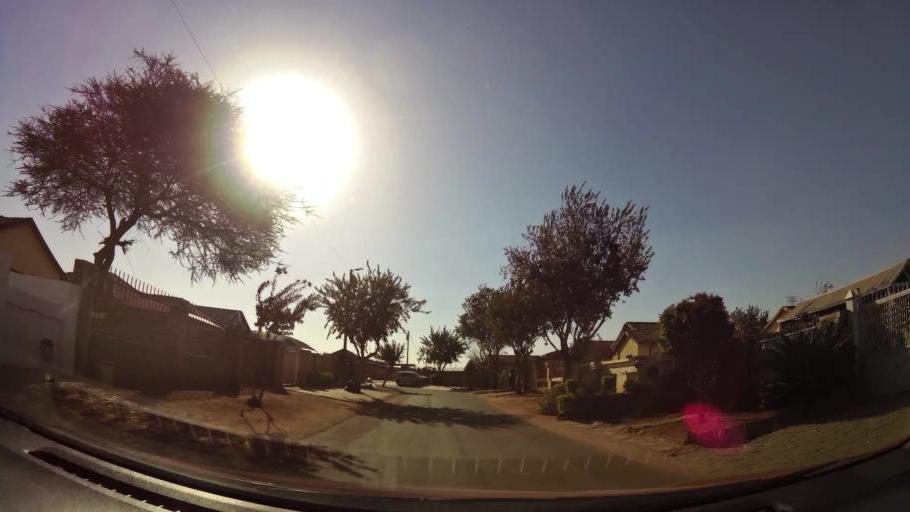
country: ZA
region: Gauteng
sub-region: City of Tshwane Metropolitan Municipality
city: Mabopane
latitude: -25.5744
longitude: 28.1015
